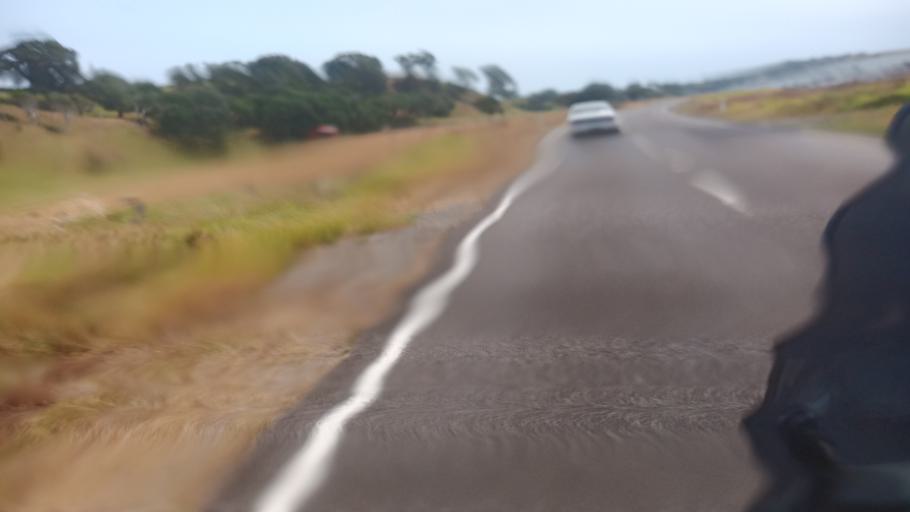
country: NZ
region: Bay of Plenty
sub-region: Opotiki District
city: Opotiki
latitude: -37.6209
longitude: 177.9270
